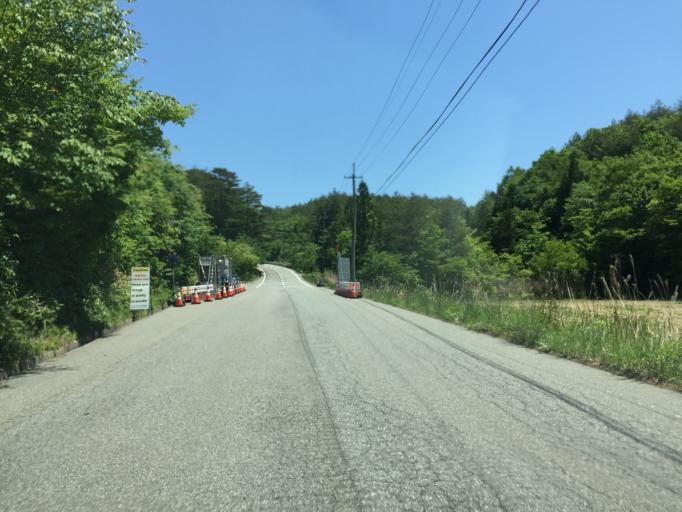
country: JP
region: Fukushima
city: Namie
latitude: 37.5217
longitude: 140.7862
